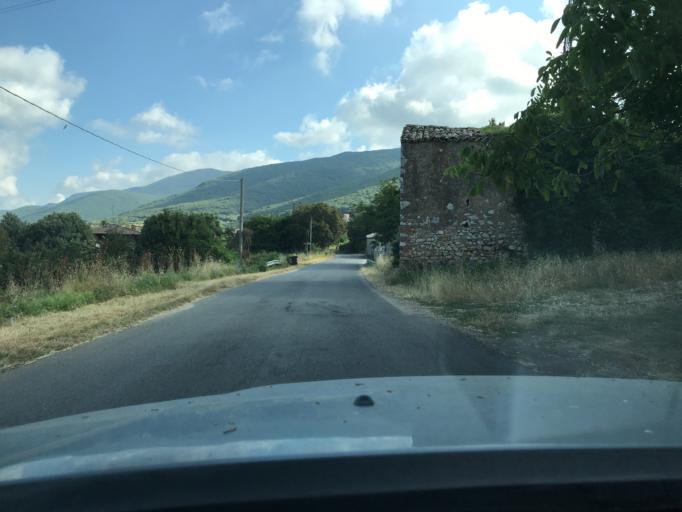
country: IT
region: Umbria
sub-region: Provincia di Terni
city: Guardea
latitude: 42.6246
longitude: 12.3158
